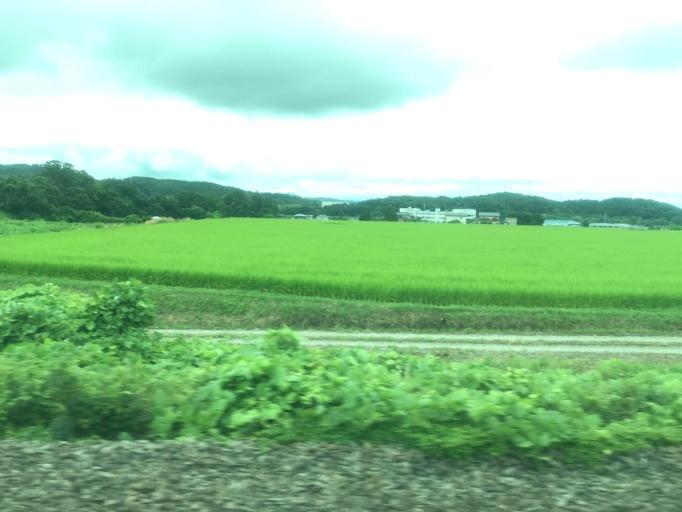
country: JP
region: Fukushima
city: Motomiya
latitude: 37.4923
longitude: 140.3945
